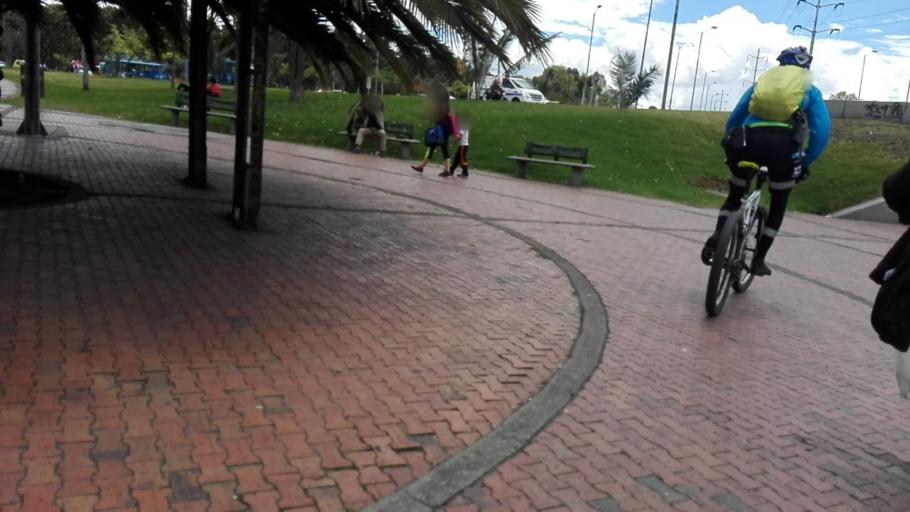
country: CO
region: Bogota D.C.
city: Bogota
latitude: 4.6722
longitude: -74.0888
